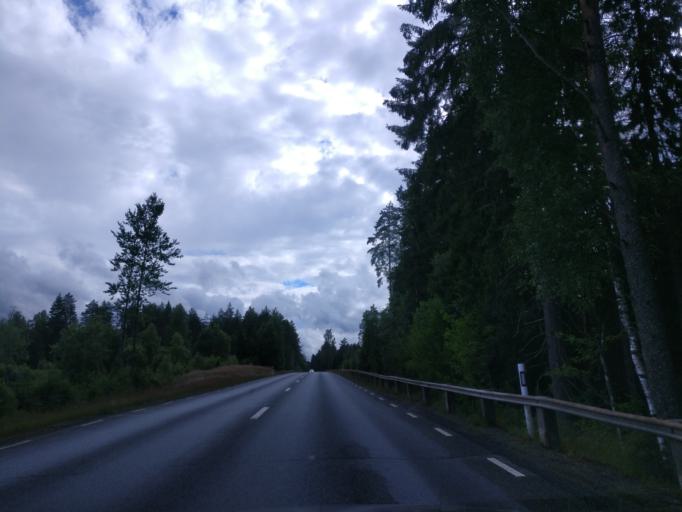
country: SE
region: Vaermland
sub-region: Hagfors Kommun
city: Hagfors
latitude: 59.9822
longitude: 13.5741
